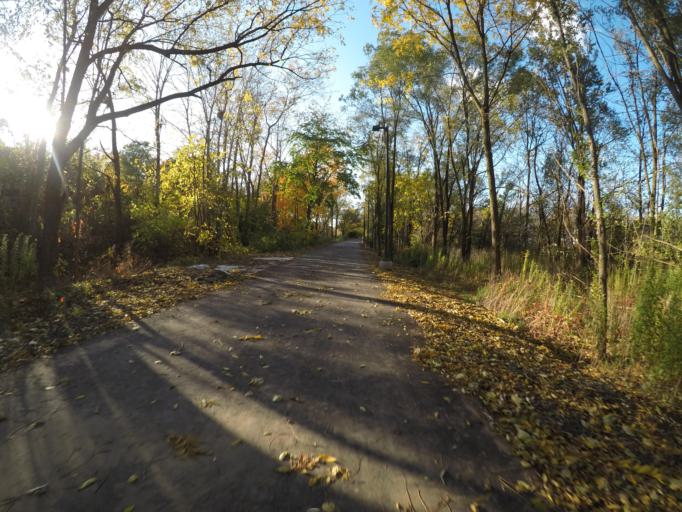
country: CA
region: Ontario
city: Kitchener
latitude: 43.4412
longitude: -80.4906
